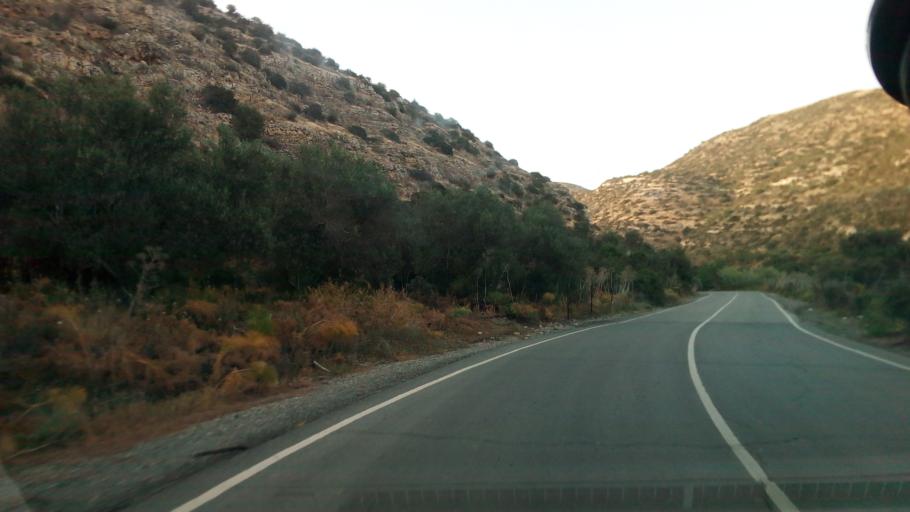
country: CY
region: Larnaka
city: Kofinou
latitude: 34.7719
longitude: 33.3992
